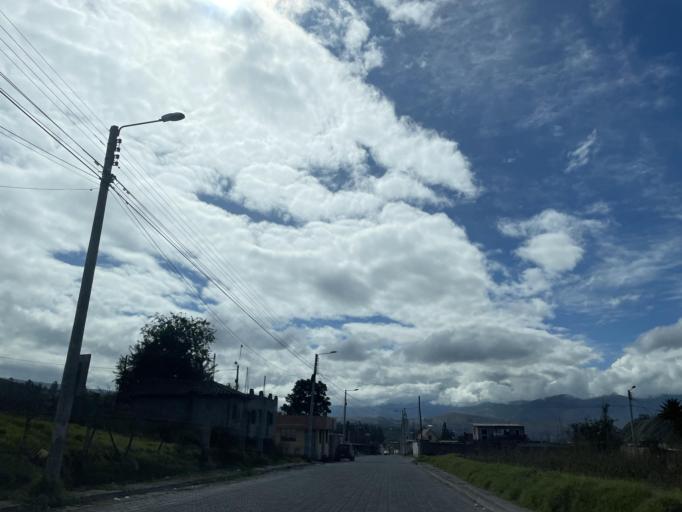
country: EC
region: Chimborazo
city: Guano
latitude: -1.6072
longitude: -78.6299
